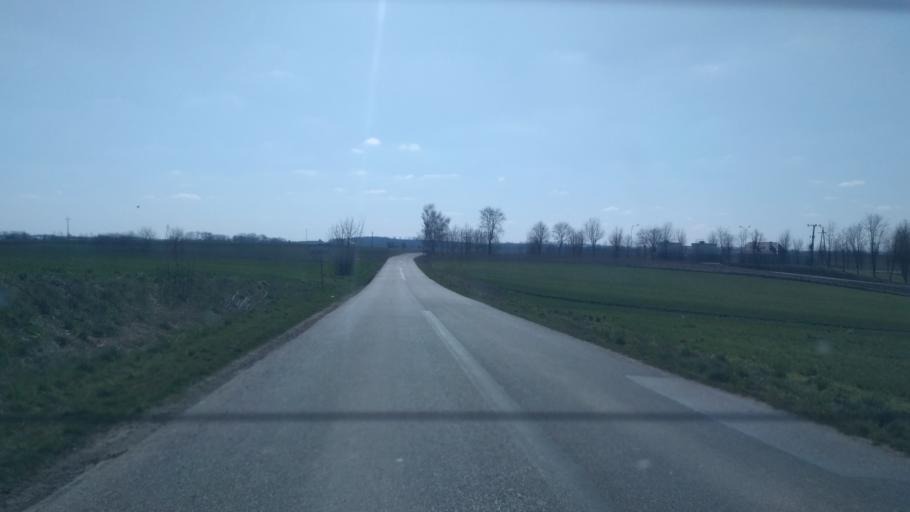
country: PL
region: Subcarpathian Voivodeship
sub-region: Powiat jaroslawski
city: Pawlosiow
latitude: 49.9541
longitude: 22.6653
